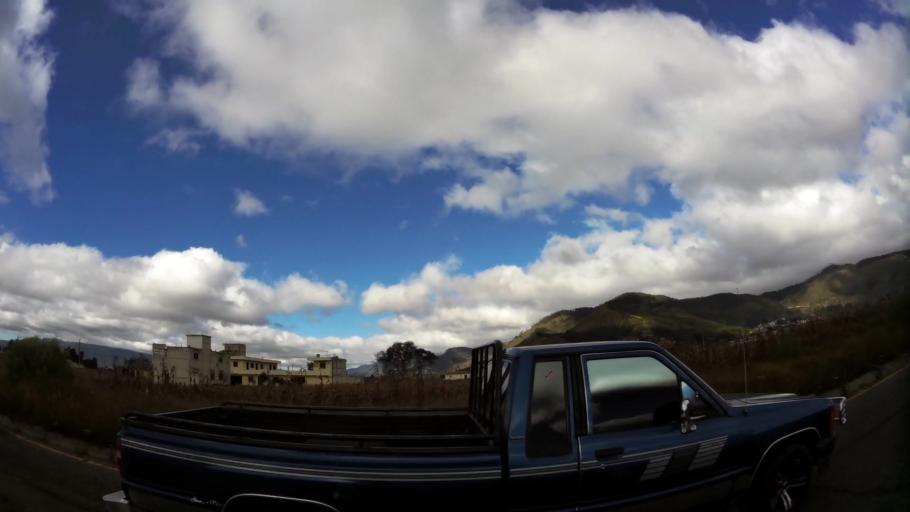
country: GT
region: Quetzaltenango
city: Salcaja
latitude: 14.8840
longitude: -91.4699
